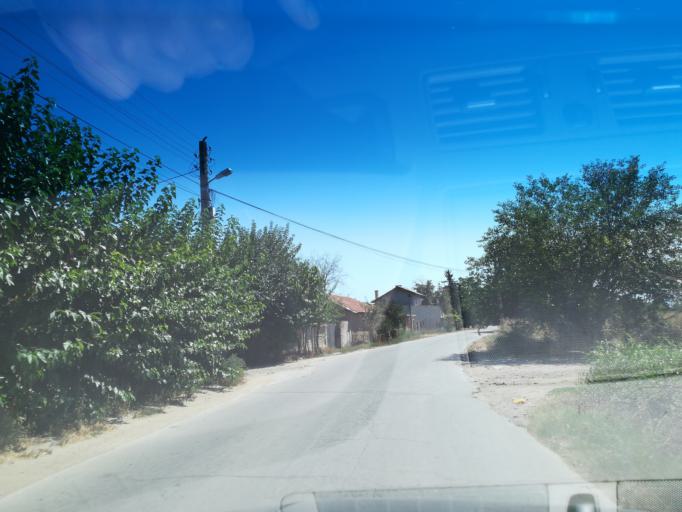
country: BG
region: Pazardzhik
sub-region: Obshtina Pazardzhik
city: Pazardzhik
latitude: 42.2692
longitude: 24.4035
